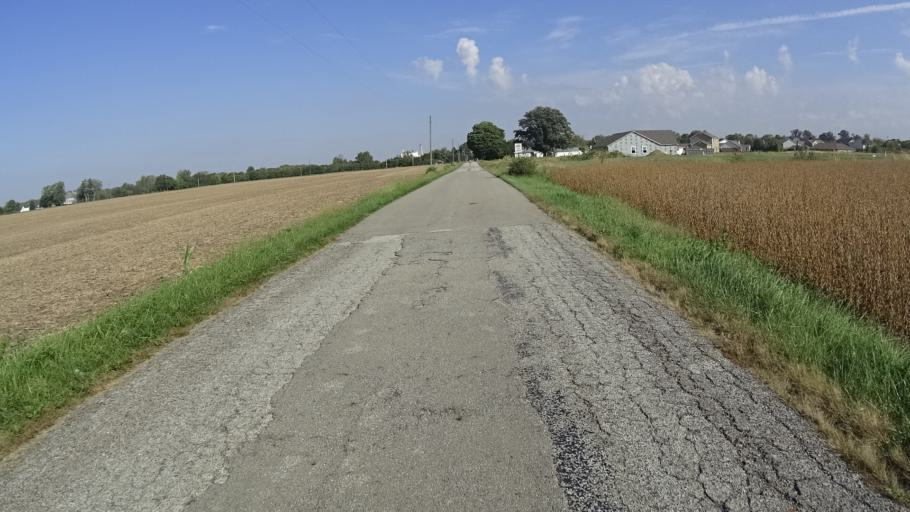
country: US
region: Indiana
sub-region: Madison County
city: Lapel
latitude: 40.0559
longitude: -85.8534
